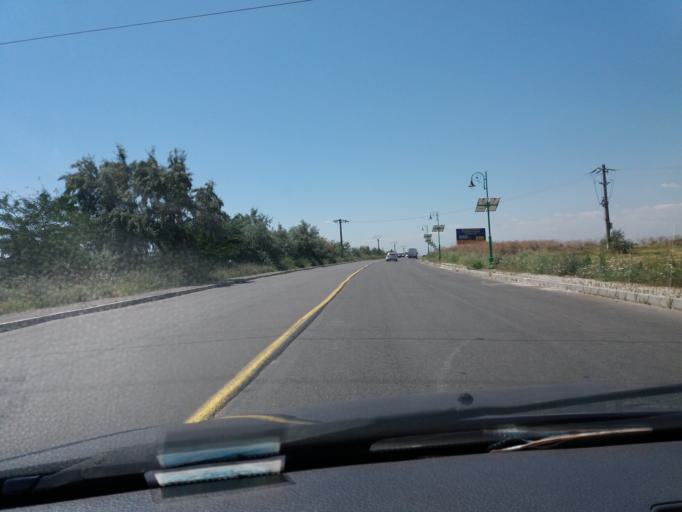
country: RO
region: Constanta
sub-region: Comuna Navodari
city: Navodari
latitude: 44.2917
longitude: 28.6110
